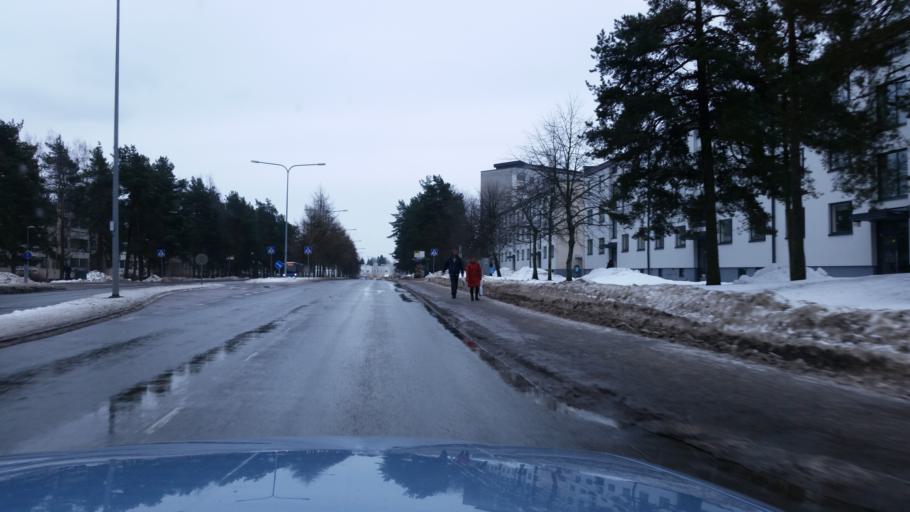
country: FI
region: Uusimaa
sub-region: Helsinki
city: Vantaa
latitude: 60.2384
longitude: 25.0770
